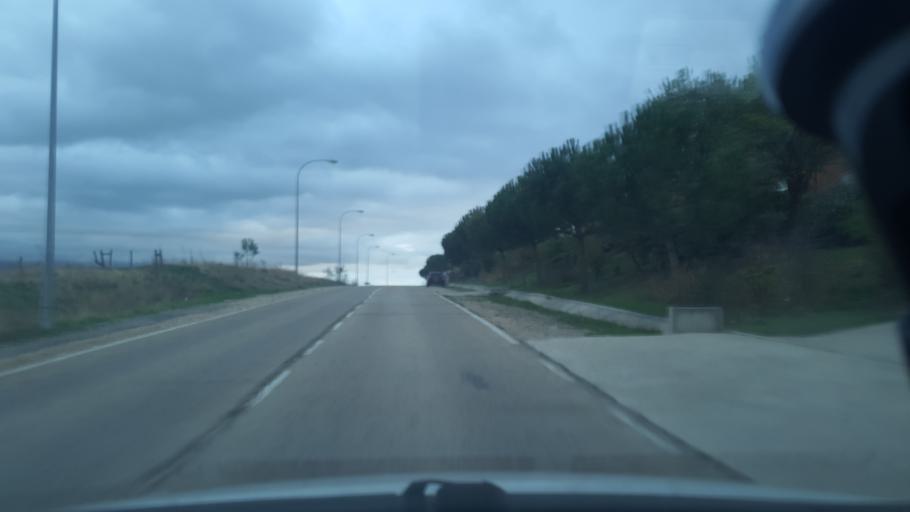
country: ES
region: Castille and Leon
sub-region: Provincia de Segovia
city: San Cristobal de Segovia
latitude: 40.9280
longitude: -4.0909
